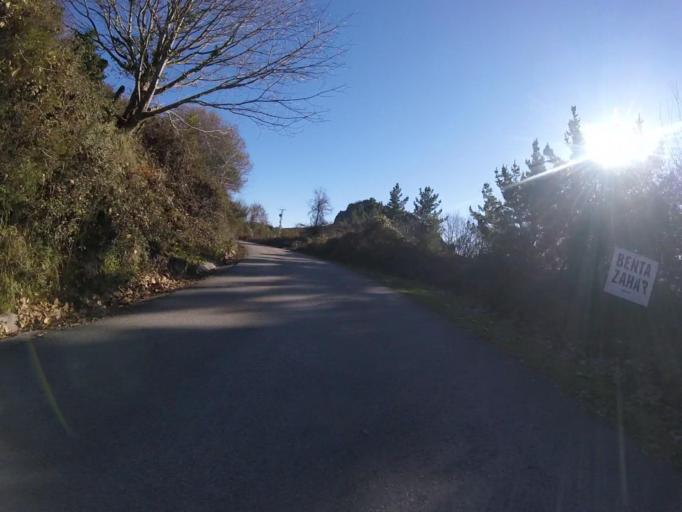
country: ES
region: Navarre
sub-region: Provincia de Navarra
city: Bera
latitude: 43.3062
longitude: -1.6811
